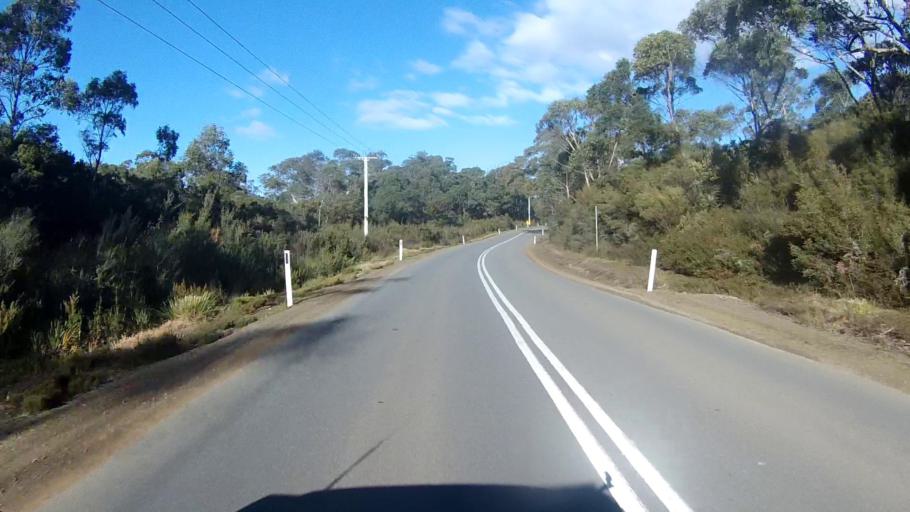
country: AU
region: Tasmania
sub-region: Clarence
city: Sandford
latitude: -43.0895
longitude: 147.8698
